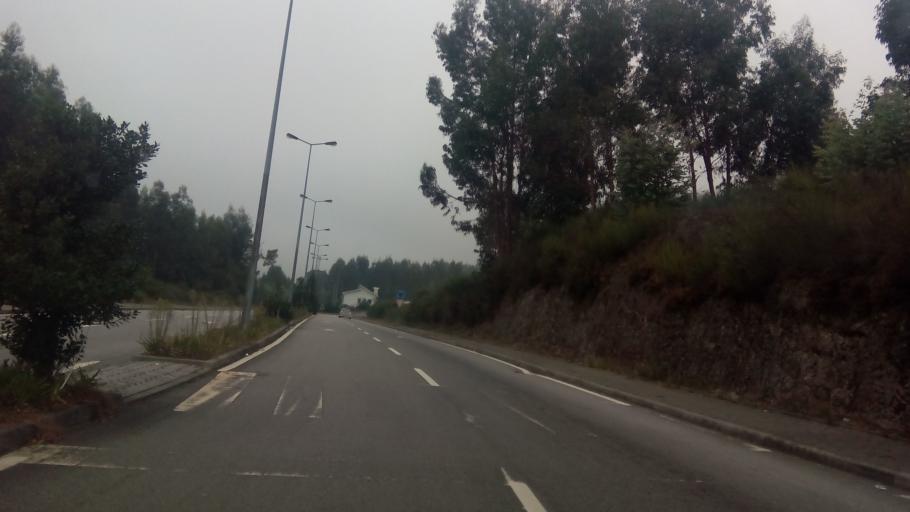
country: PT
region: Porto
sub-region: Paredes
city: Baltar
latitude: 41.1924
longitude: -8.4027
